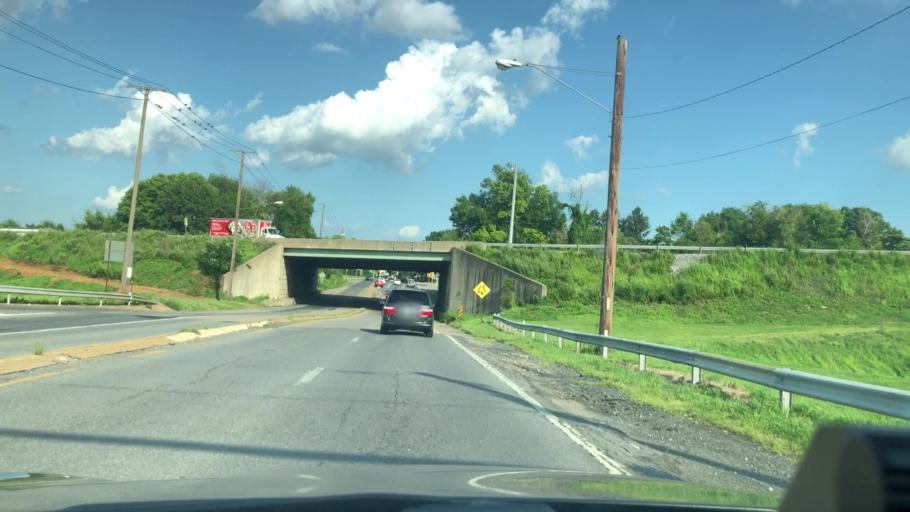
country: US
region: Pennsylvania
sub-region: Lehigh County
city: Allentown
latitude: 40.6189
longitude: -75.5025
